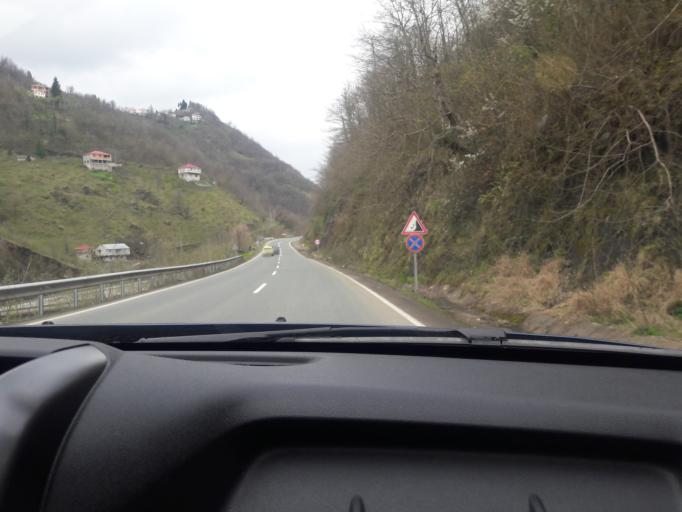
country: TR
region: Trabzon
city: Salpazari
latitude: 40.9836
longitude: 39.1954
